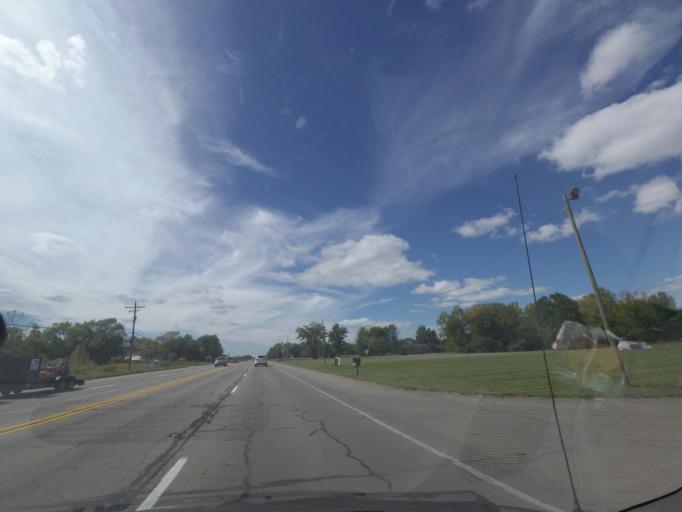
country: US
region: Indiana
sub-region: Hancock County
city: New Palestine
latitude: 39.7806
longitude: -85.8712
